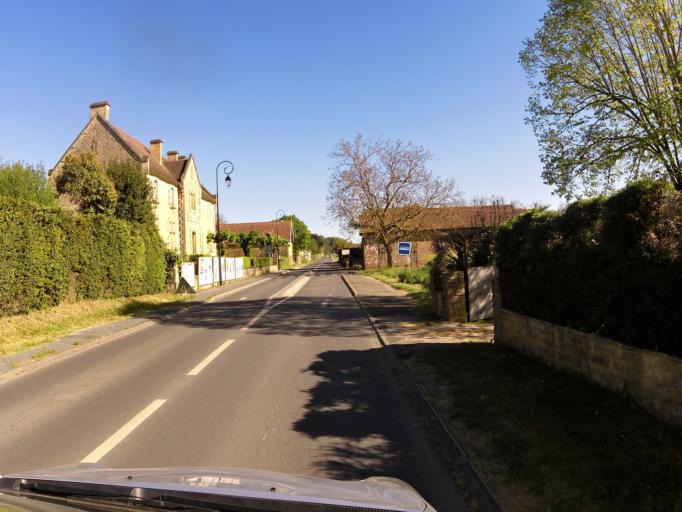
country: FR
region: Aquitaine
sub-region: Departement de la Dordogne
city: Cenac-et-Saint-Julien
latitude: 44.8222
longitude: 1.1879
